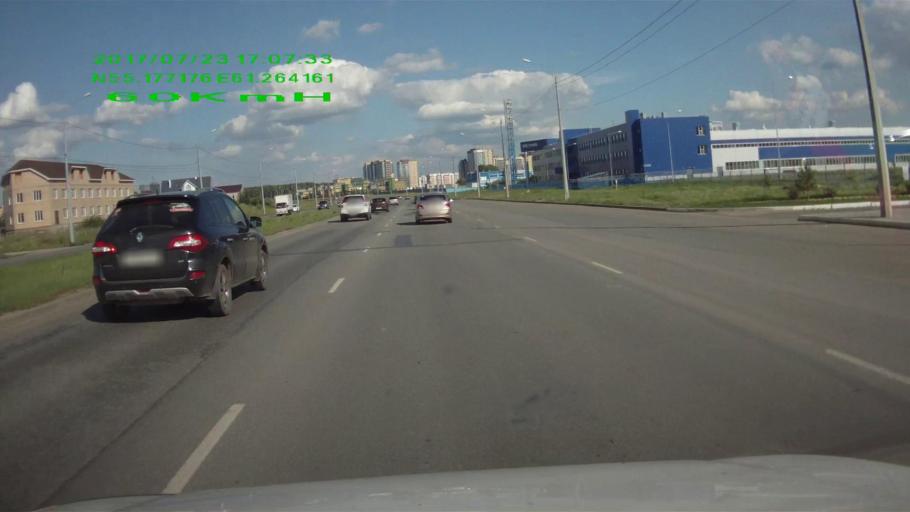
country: RU
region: Chelyabinsk
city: Roshchino
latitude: 55.1769
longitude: 61.2652
